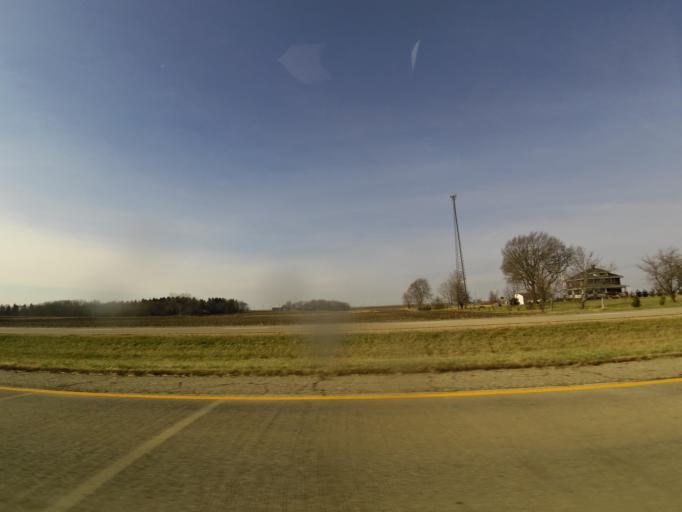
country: US
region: Illinois
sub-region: Macon County
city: Forsyth
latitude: 39.9656
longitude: -88.9559
